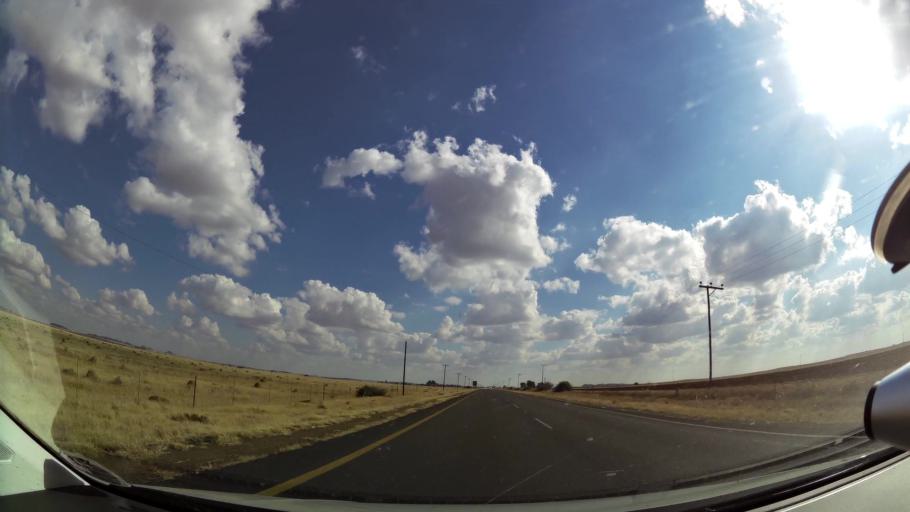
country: ZA
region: Orange Free State
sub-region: Xhariep District Municipality
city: Koffiefontein
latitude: -29.1299
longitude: 25.5121
